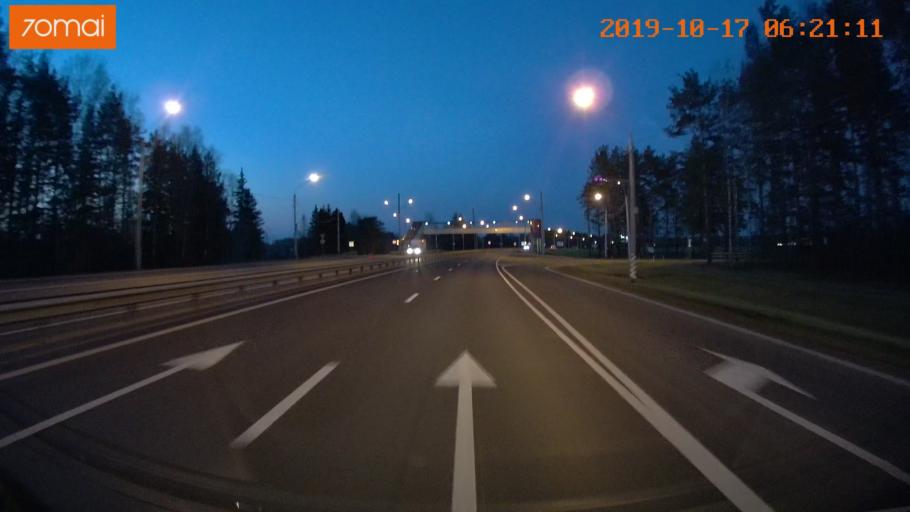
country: RU
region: Ivanovo
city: Lezhnevo
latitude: 56.8053
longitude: 40.8870
